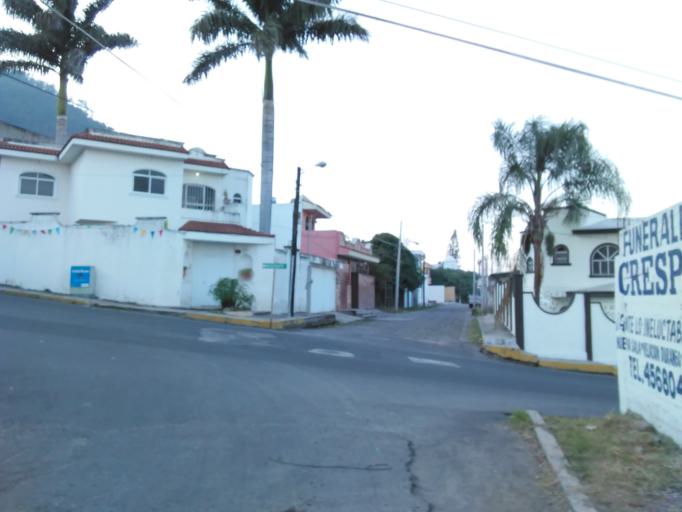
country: MX
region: Nayarit
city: Tepic
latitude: 21.5065
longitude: -104.9197
